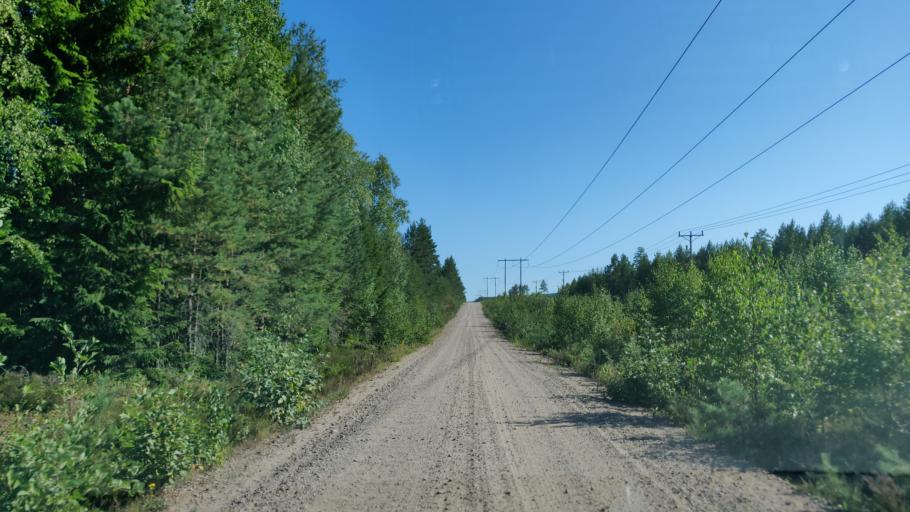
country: SE
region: Vaermland
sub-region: Hagfors Kommun
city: Ekshaerad
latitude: 60.0635
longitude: 13.5203
